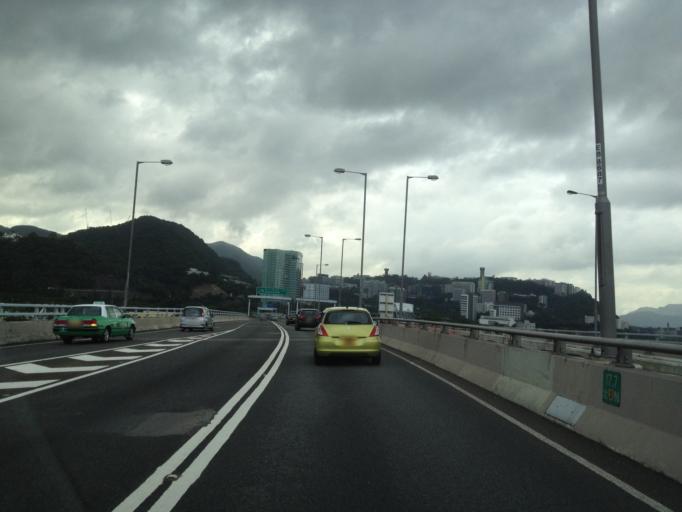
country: HK
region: Sha Tin
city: Sha Tin
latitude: 22.4061
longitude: 114.2177
